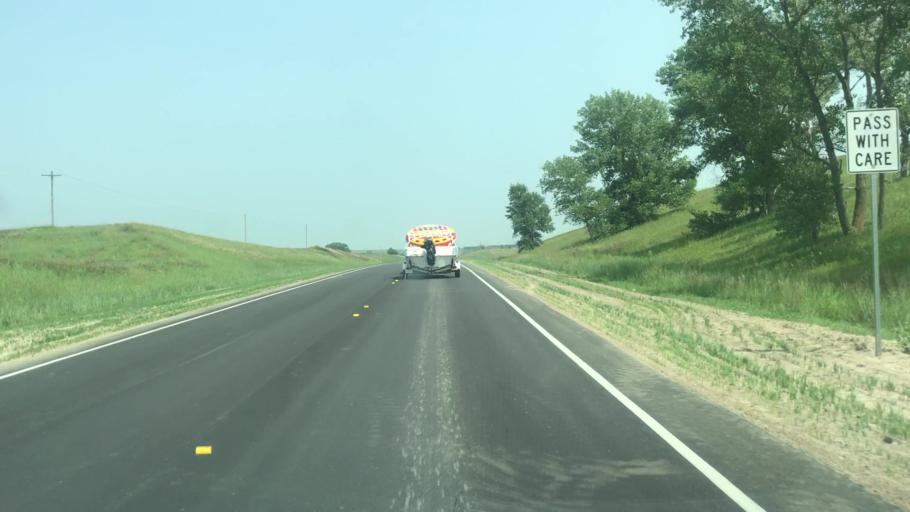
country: US
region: Nebraska
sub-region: Sherman County
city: Loup City
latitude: 41.2631
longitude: -98.9294
